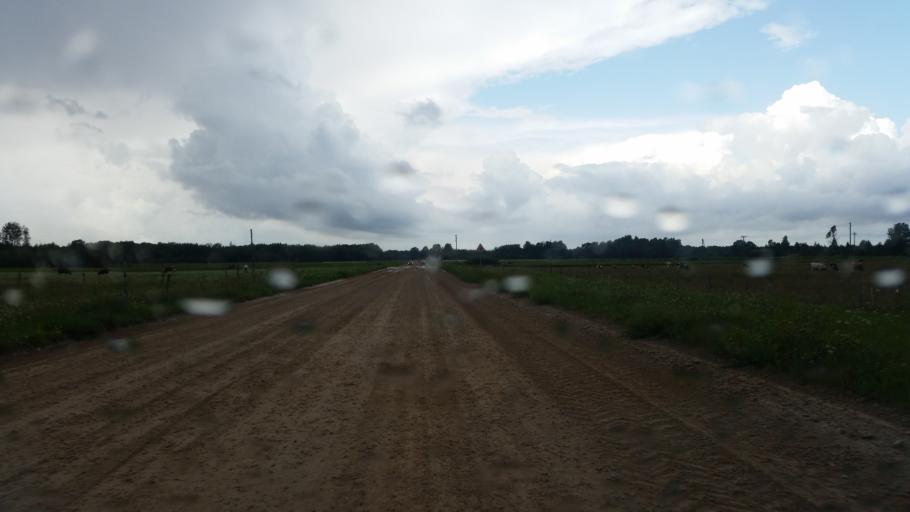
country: LV
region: Vecumnieki
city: Vecumnieki
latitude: 56.4279
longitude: 24.4638
